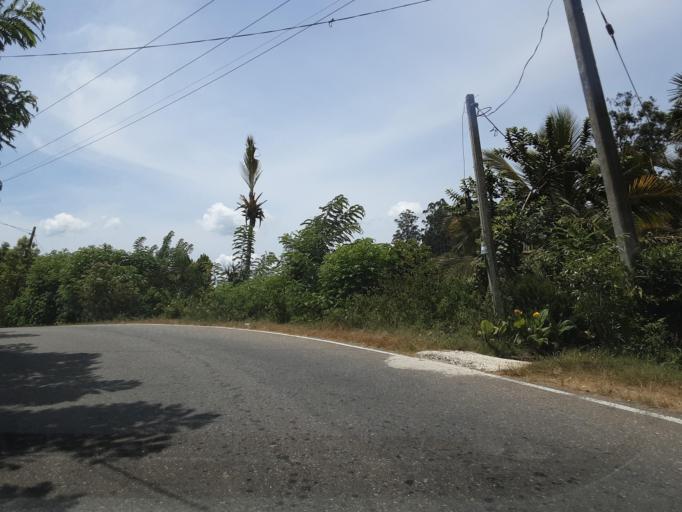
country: LK
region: Uva
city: Badulla
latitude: 6.9606
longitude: 80.9365
